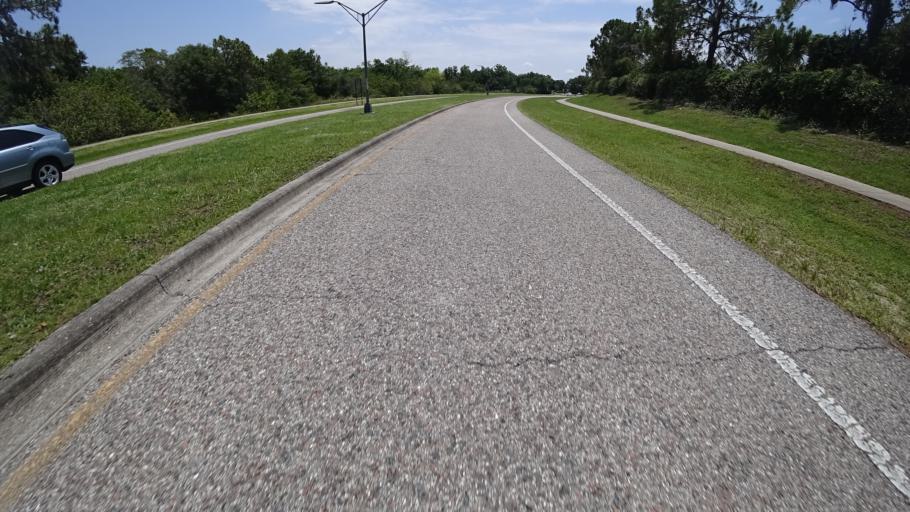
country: US
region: Florida
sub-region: Sarasota County
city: Desoto Lakes
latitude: 27.4138
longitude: -82.4667
